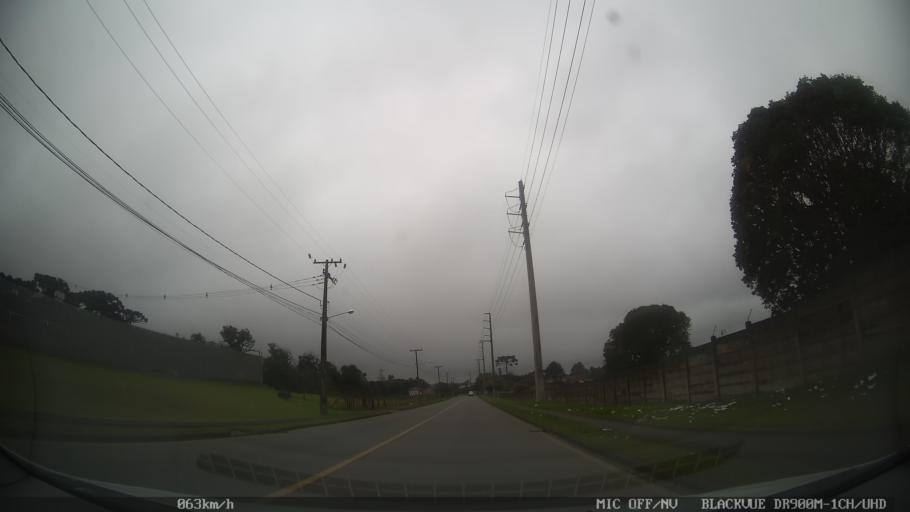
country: BR
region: Parana
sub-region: Sao Jose Dos Pinhais
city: Sao Jose dos Pinhais
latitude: -25.5796
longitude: -49.1703
